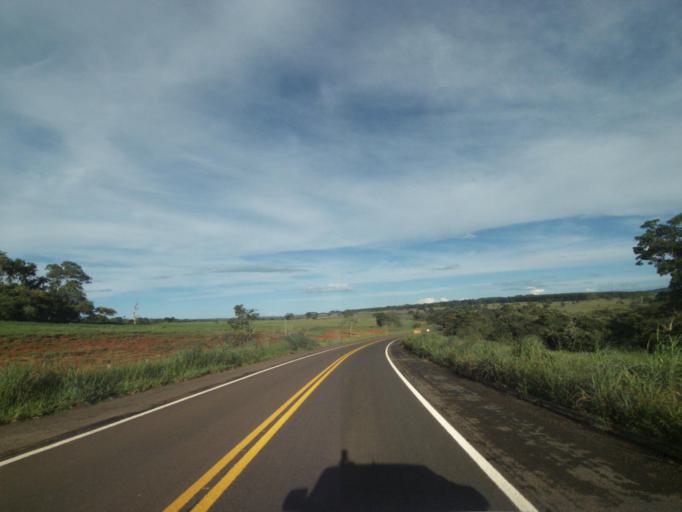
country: BR
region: Goias
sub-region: Itaberai
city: Itaberai
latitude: -15.9076
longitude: -49.5700
